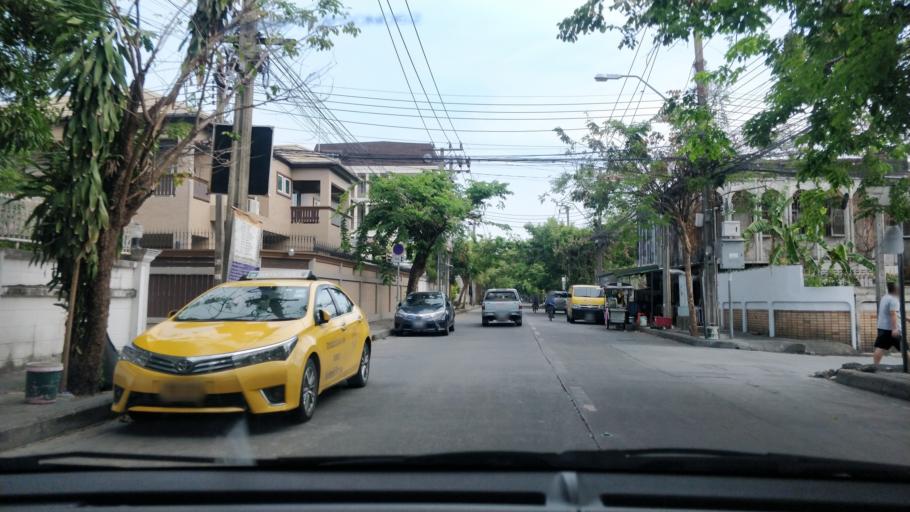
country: TH
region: Bangkok
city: Bang Kapi
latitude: 13.7456
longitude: 100.6316
